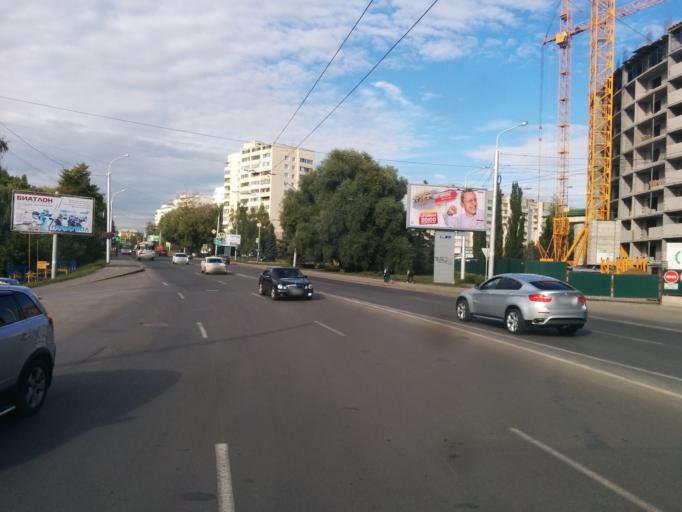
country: RU
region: Bashkortostan
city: Ufa
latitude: 54.8118
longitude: 56.0562
